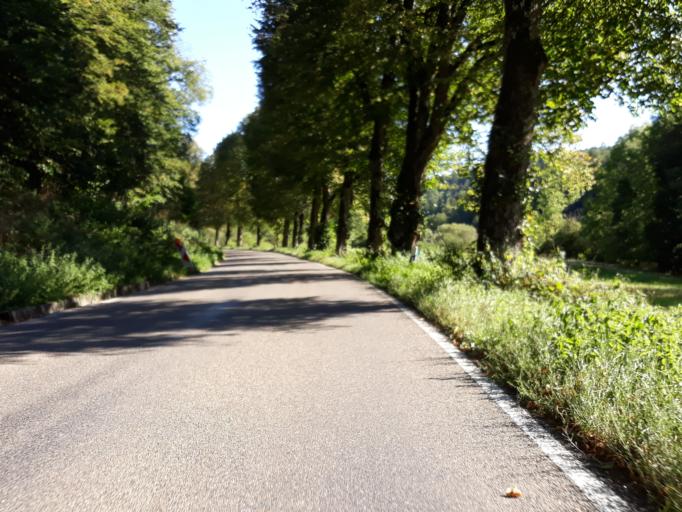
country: DE
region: Baden-Wuerttemberg
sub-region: Regierungsbezirk Stuttgart
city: Aidlingen
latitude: 48.6732
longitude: 8.9118
